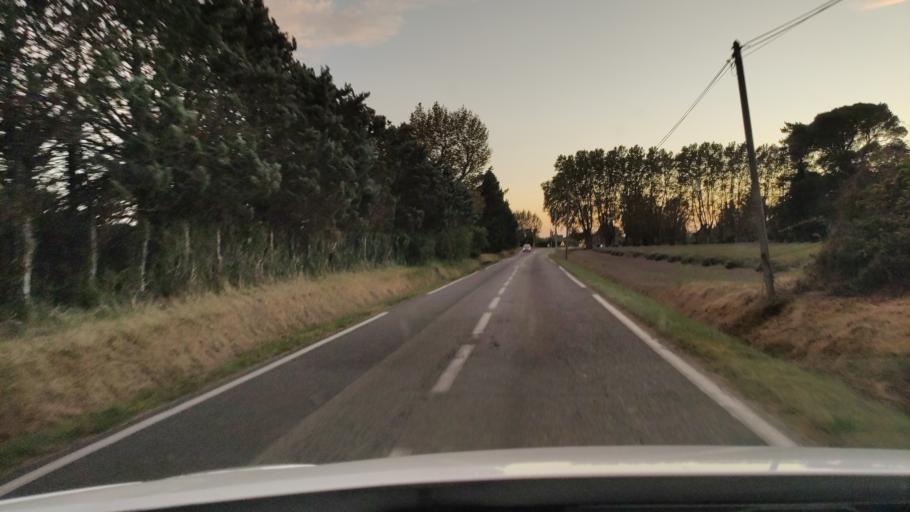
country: FR
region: Provence-Alpes-Cote d'Azur
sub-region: Departement du Vaucluse
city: Le Thor
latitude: 43.9409
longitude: 5.0057
